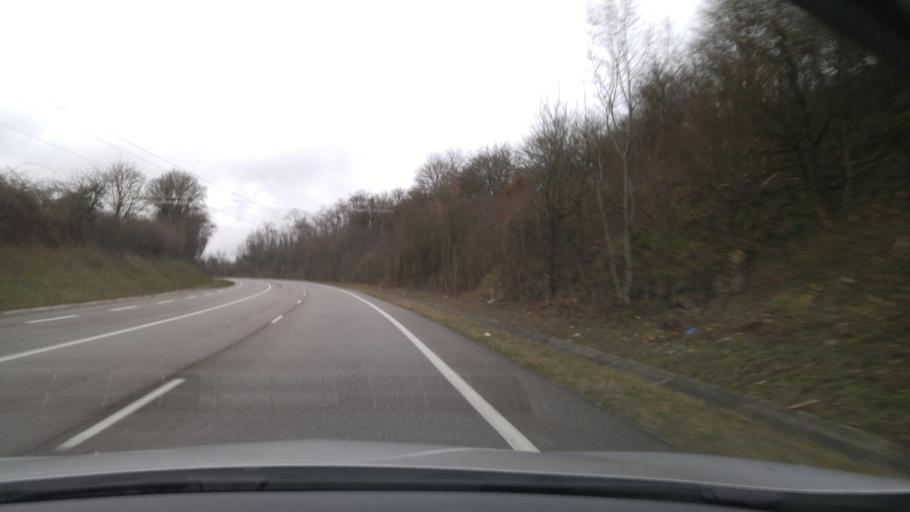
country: FR
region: Rhone-Alpes
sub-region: Departement de l'Isere
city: La Verpilliere
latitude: 45.6359
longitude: 5.1253
